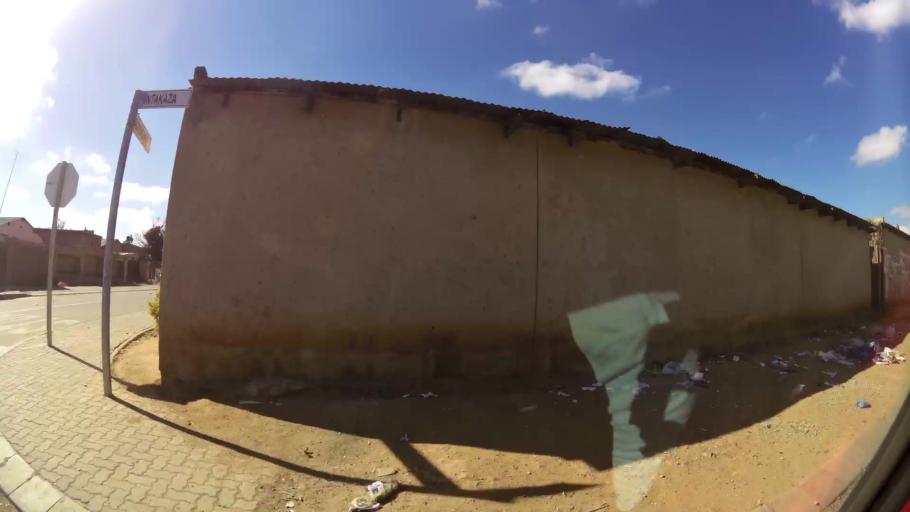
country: ZA
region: Gauteng
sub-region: City of Johannesburg Metropolitan Municipality
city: Midrand
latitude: -26.0311
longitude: 28.1691
